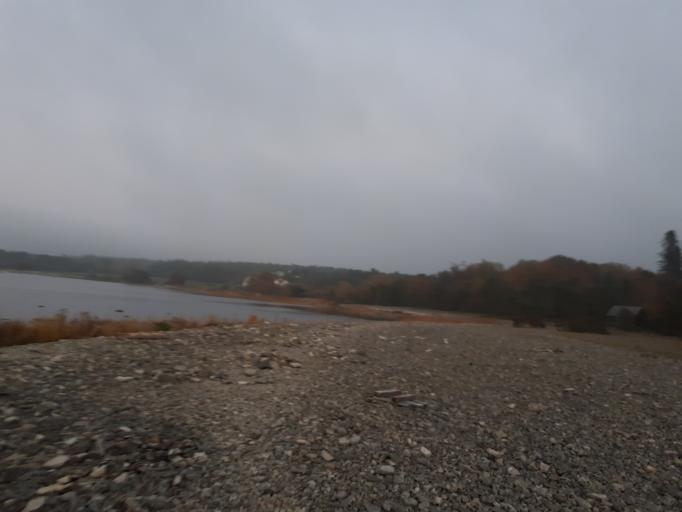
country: SE
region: Gotland
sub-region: Gotland
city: Visby
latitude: 57.6891
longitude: 18.3482
